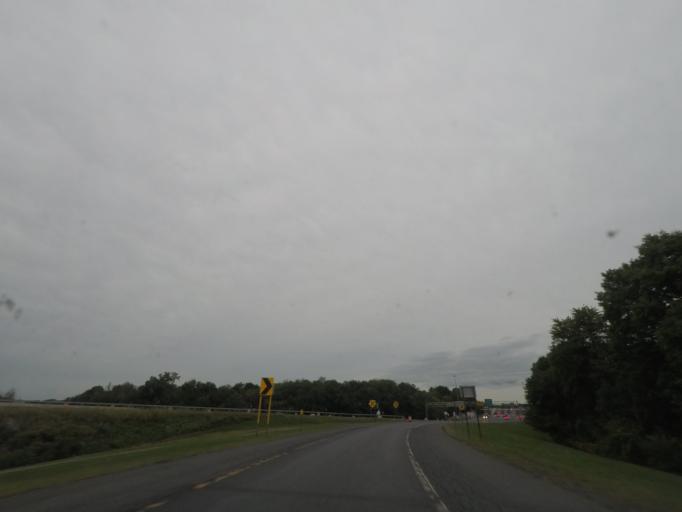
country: US
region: New York
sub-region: Columbia County
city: Niverville
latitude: 42.4832
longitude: -73.6693
